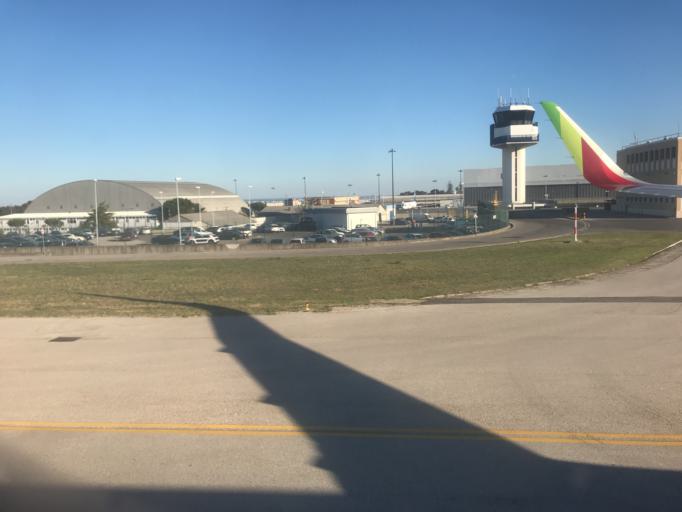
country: PT
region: Lisbon
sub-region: Loures
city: Camarate
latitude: 38.7816
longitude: -9.1334
